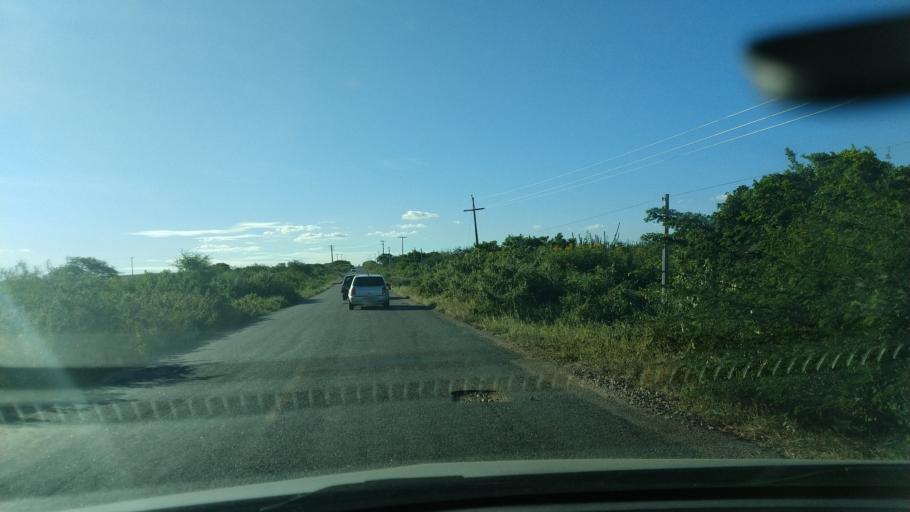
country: BR
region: Rio Grande do Norte
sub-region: Sao Jose Do Campestre
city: Sao Jose do Campestre
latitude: -6.4118
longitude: -35.6517
